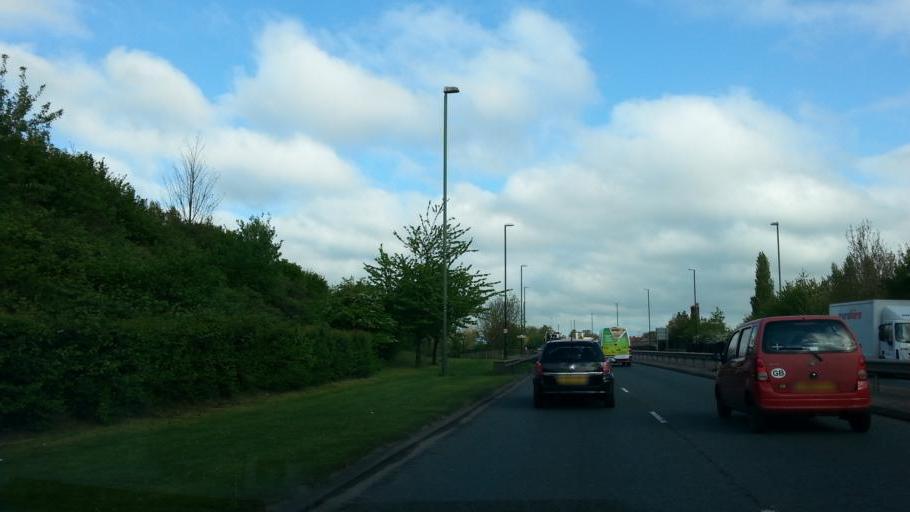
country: GB
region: England
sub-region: Warwickshire
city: Exhall
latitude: 52.4330
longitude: -1.4891
